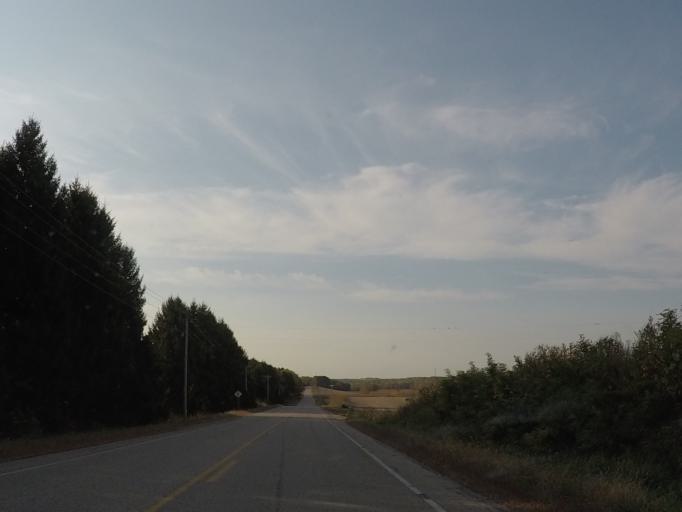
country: US
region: Wisconsin
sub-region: Dane County
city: Cross Plains
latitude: 43.0411
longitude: -89.6163
